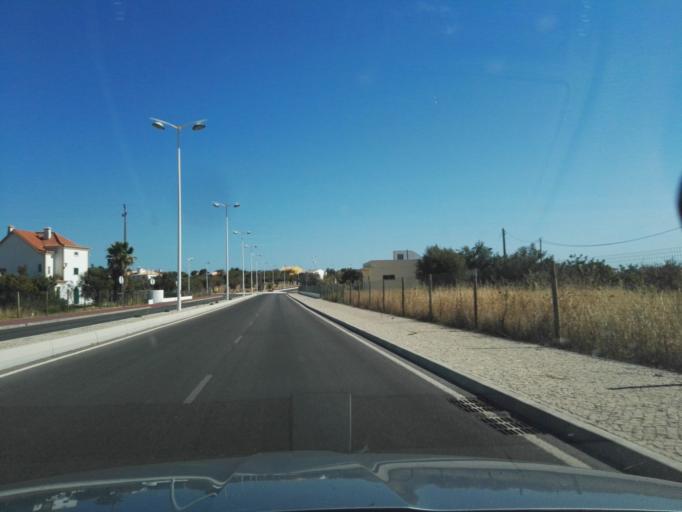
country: PT
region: Faro
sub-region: Sao Bras de Alportel
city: Sao Bras de Alportel
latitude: 37.1554
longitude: -7.8775
